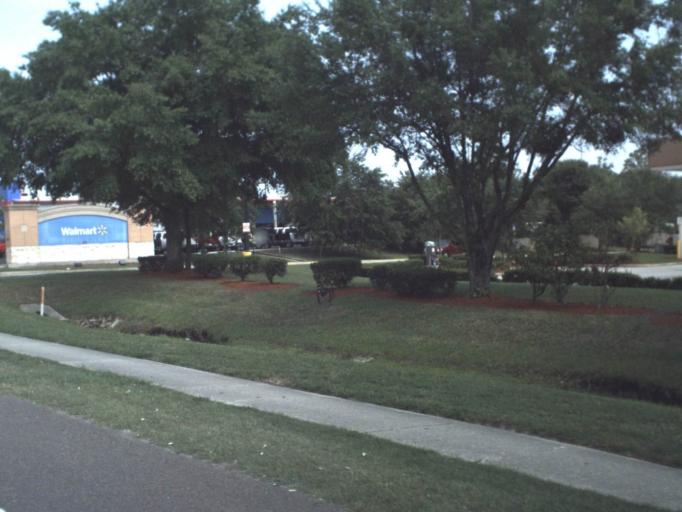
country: US
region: Florida
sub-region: Duval County
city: Jacksonville
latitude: 30.2868
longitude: -81.5632
